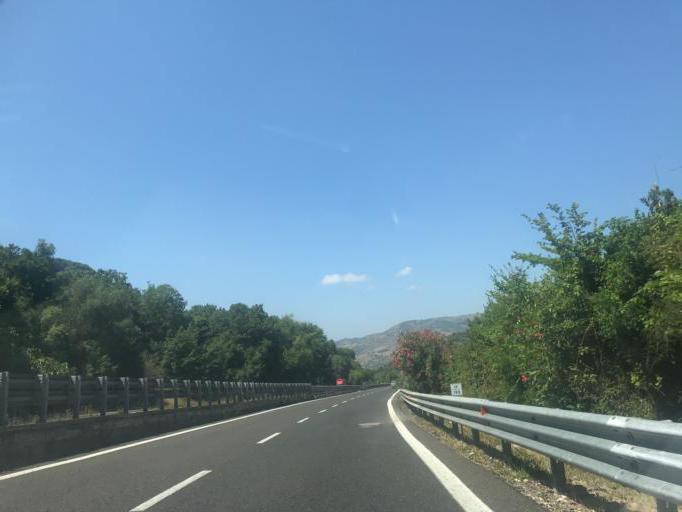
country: IT
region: Sardinia
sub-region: Provincia di Sassari
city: Florinas
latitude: 40.6552
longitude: 8.6716
